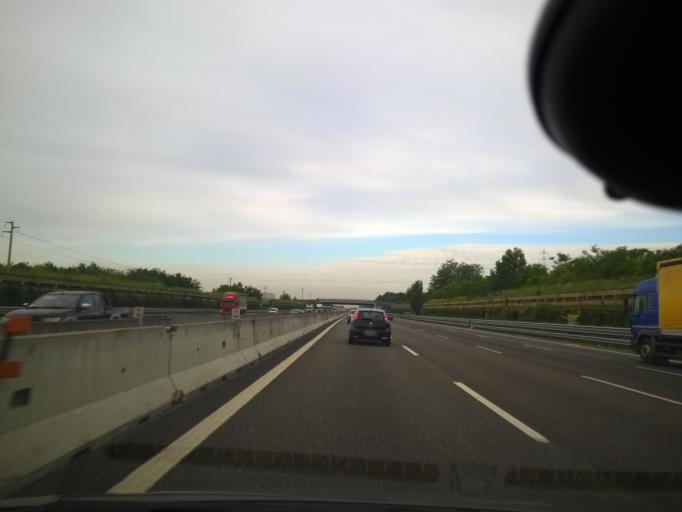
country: IT
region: Lombardy
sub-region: Citta metropolitana di Milano
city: Cambiago
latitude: 45.5852
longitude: 9.4472
